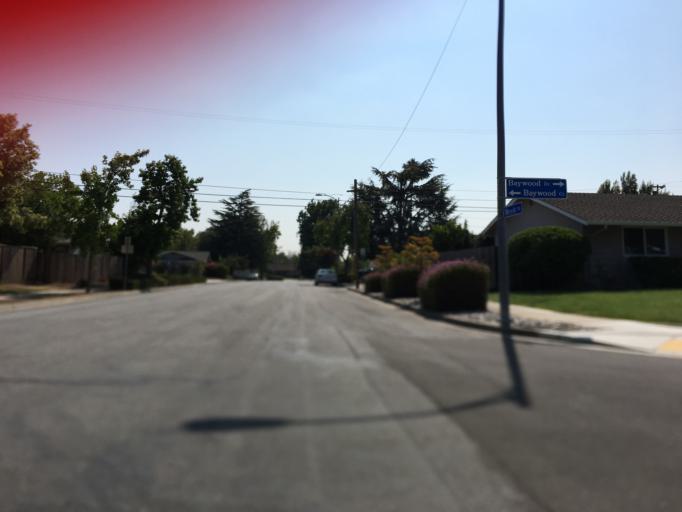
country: US
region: California
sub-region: Santa Clara County
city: Cupertino
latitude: 37.3302
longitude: -122.0222
